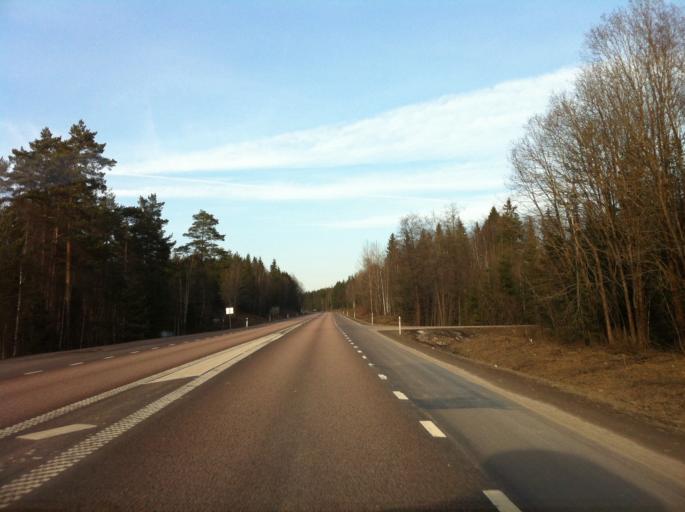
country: SE
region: Vaermland
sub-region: Filipstads Kommun
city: Filipstad
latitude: 59.7383
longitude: 14.2276
